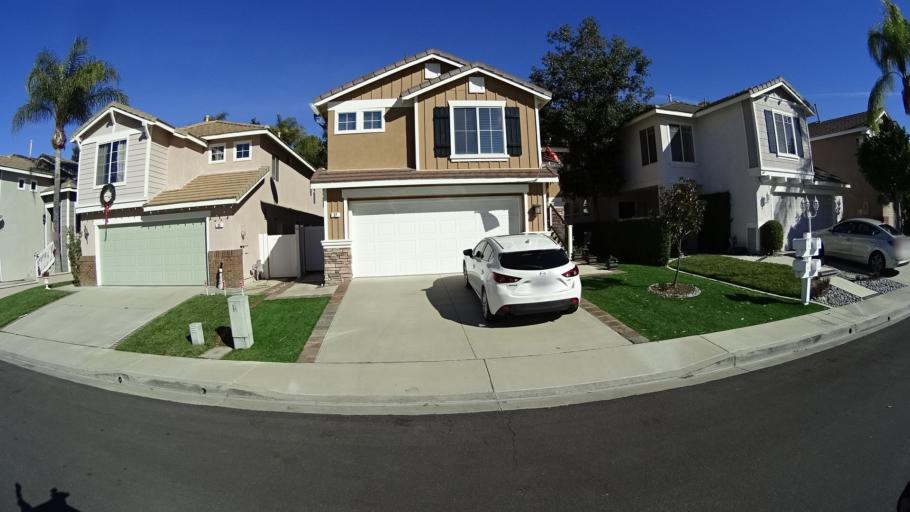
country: US
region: California
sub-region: Orange County
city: Coto De Caza
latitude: 33.5899
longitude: -117.5945
